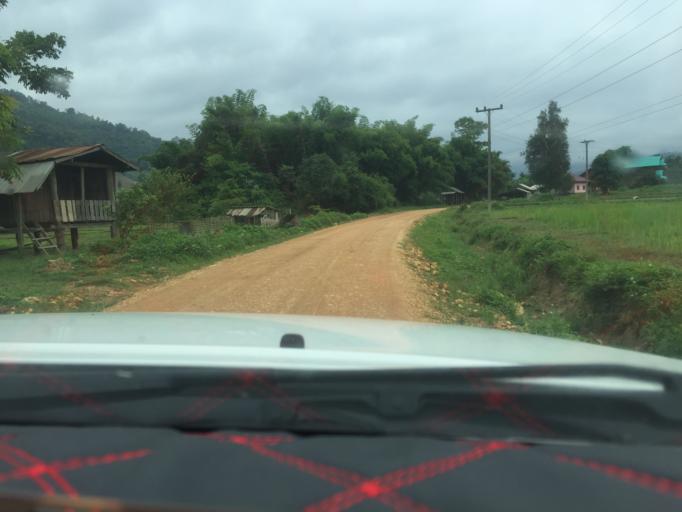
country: TH
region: Phayao
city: Phu Sang
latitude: 19.6825
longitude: 100.5022
